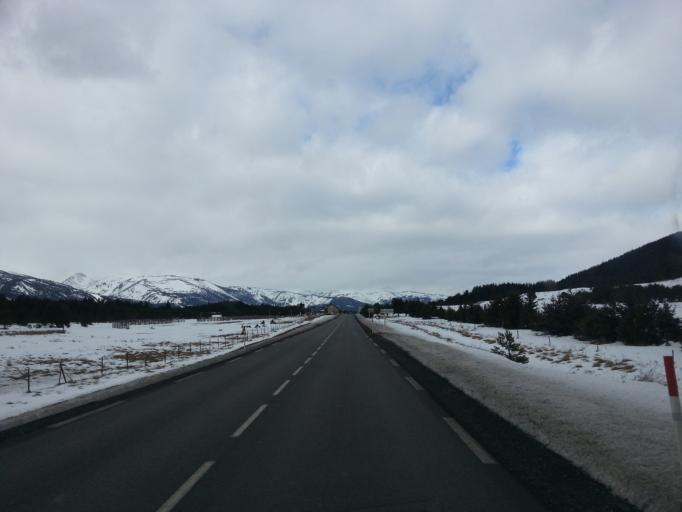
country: ES
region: Catalonia
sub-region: Provincia de Girona
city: Llivia
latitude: 42.5453
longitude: 2.1163
